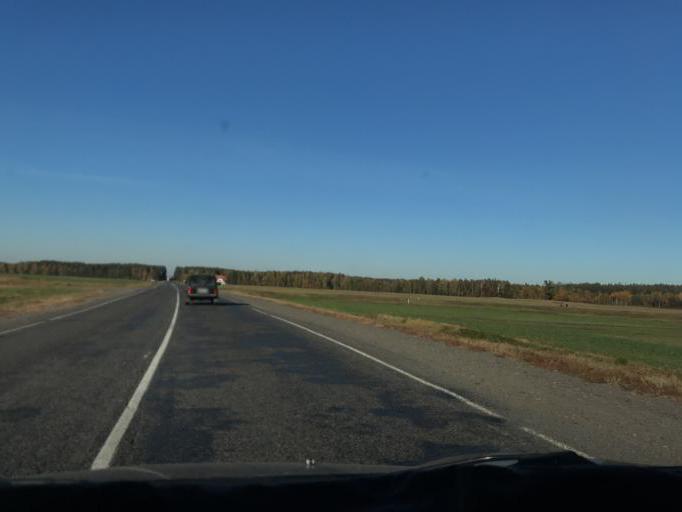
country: BY
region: Gomel
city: Kalinkavichy
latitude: 52.0461
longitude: 29.3611
